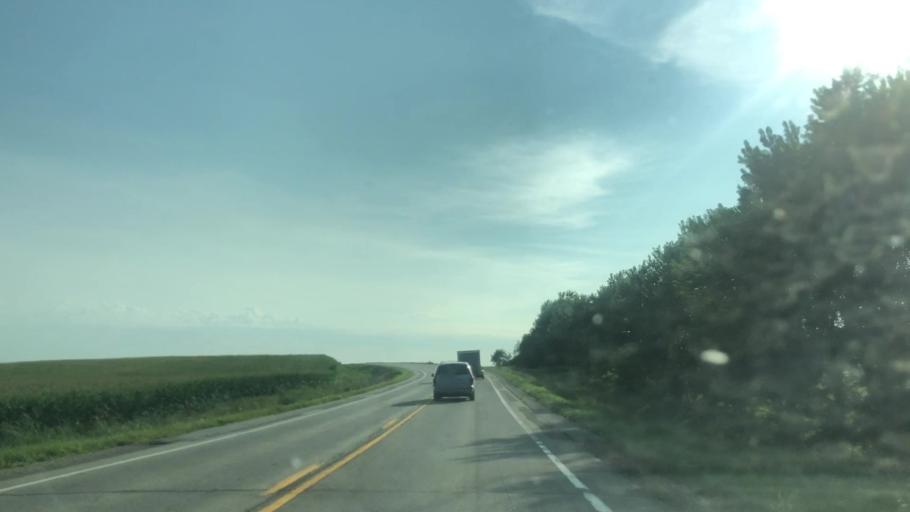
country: US
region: Iowa
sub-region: Marshall County
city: Marshalltown
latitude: 42.0231
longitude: -93.0069
